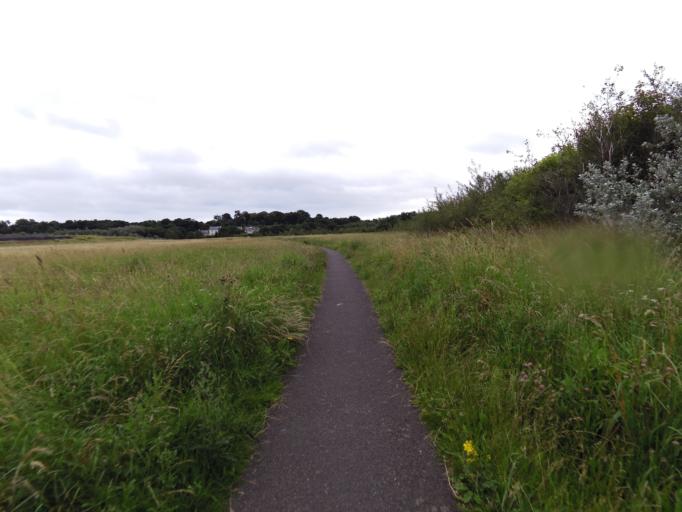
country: GB
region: Scotland
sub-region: East Lothian
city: Musselburgh
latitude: 55.9509
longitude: -3.0225
